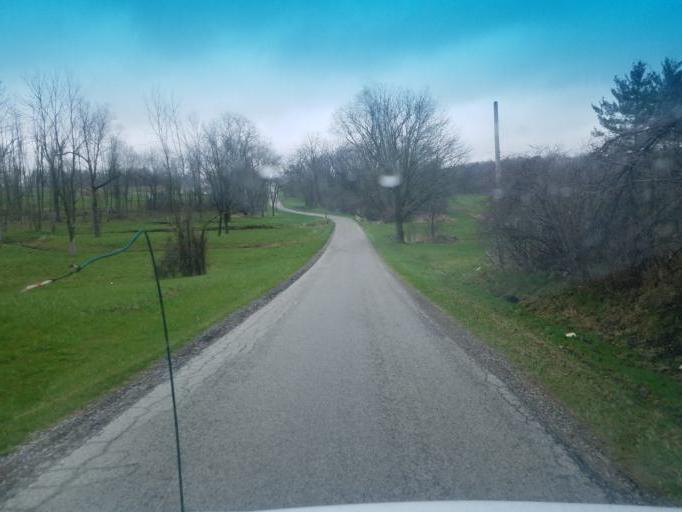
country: US
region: Ohio
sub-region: Huron County
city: Plymouth
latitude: 40.9622
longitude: -82.7386
